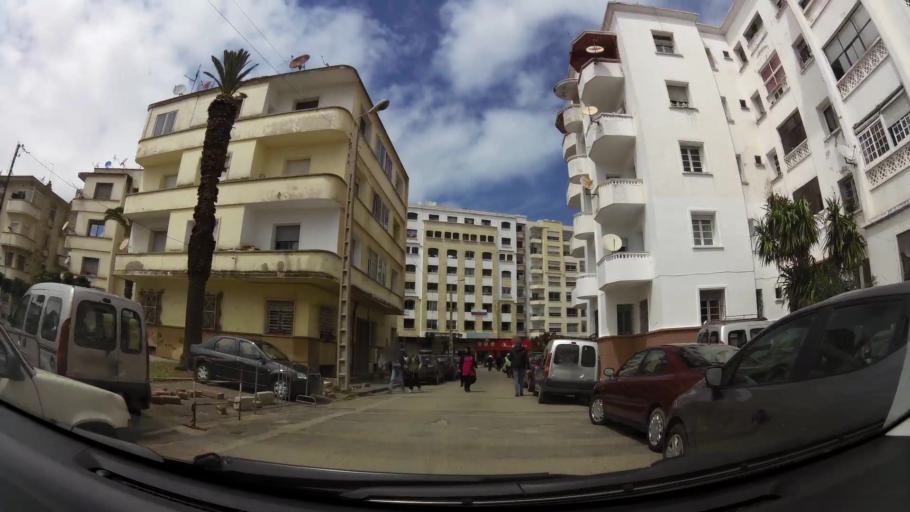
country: MA
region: Grand Casablanca
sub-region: Casablanca
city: Casablanca
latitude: 33.5950
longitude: -7.6389
